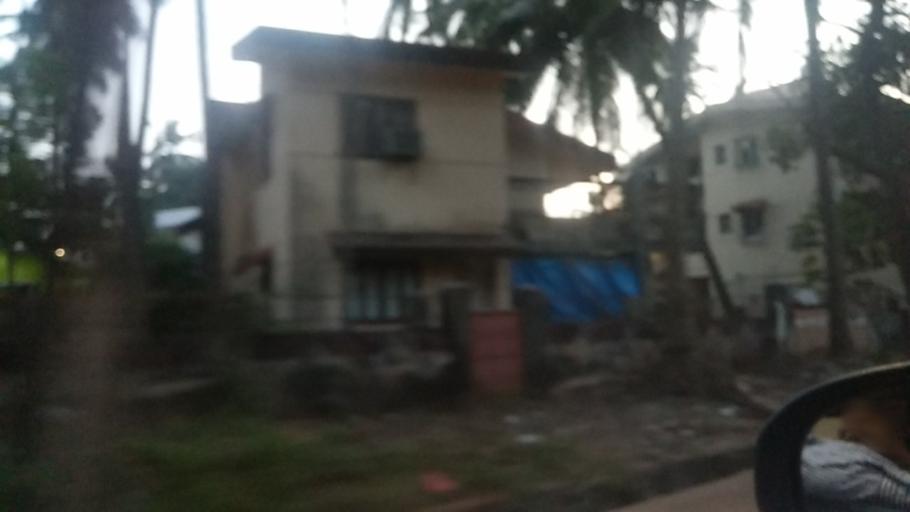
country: IN
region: Goa
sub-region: North Goa
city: Taleigao
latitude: 15.4700
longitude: 73.8245
